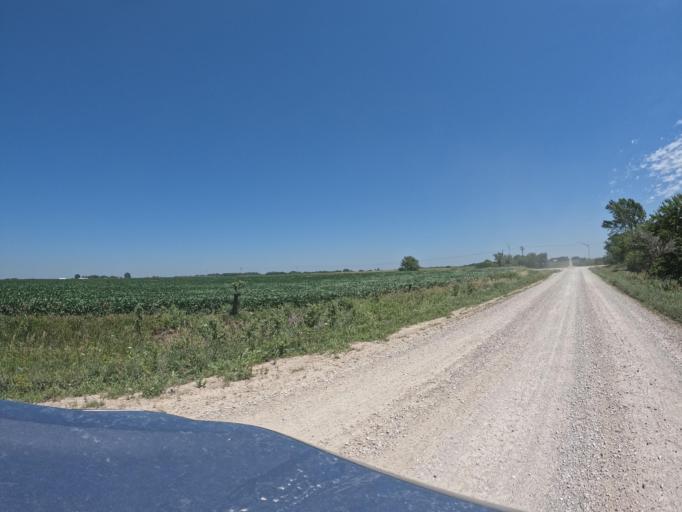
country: US
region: Iowa
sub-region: Keokuk County
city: Sigourney
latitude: 41.4523
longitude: -92.3567
